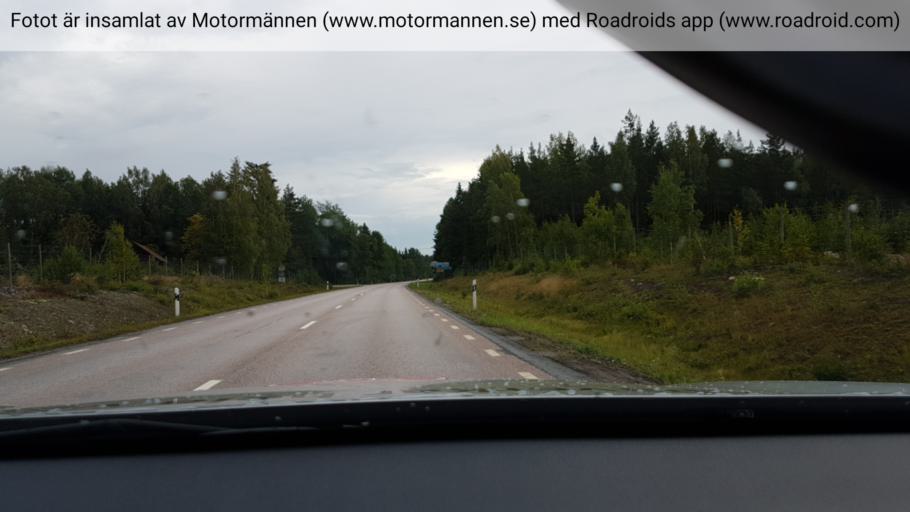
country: SE
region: Uppsala
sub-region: Osthammars Kommun
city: Osterbybruk
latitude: 60.4229
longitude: 17.8489
